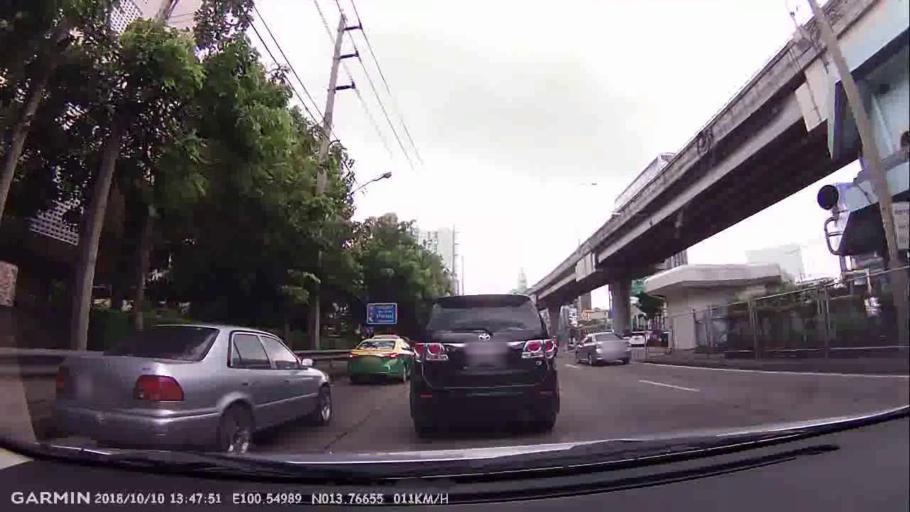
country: TH
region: Bangkok
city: Din Daeng
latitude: 13.7666
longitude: 100.5499
